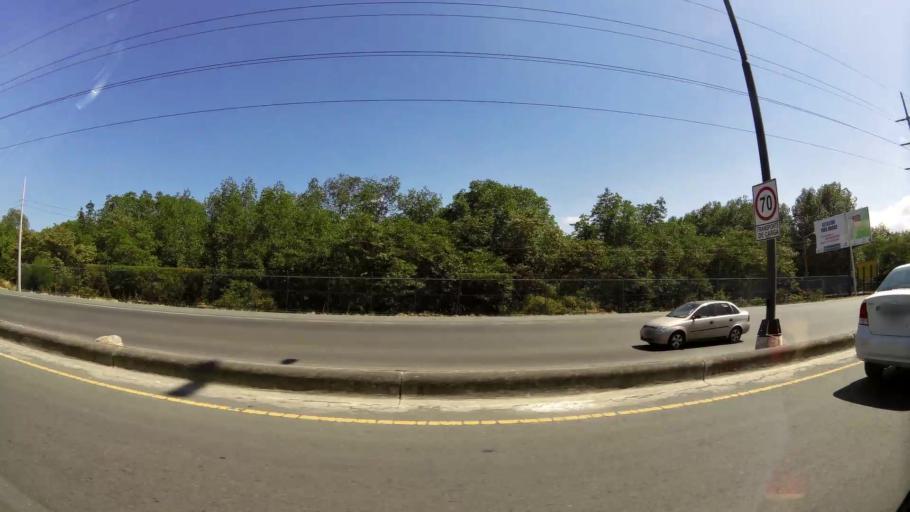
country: EC
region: Guayas
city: Guayaquil
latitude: -2.2259
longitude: -79.9561
